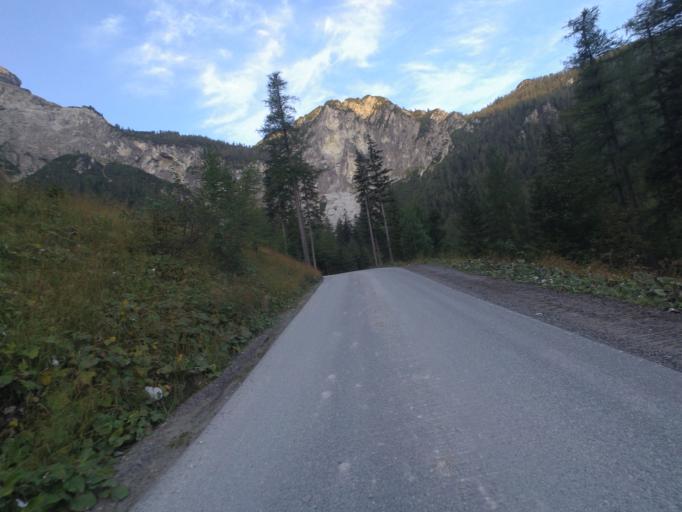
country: AT
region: Salzburg
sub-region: Politischer Bezirk Sankt Johann im Pongau
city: Untertauern
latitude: 47.2370
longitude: 13.4230
